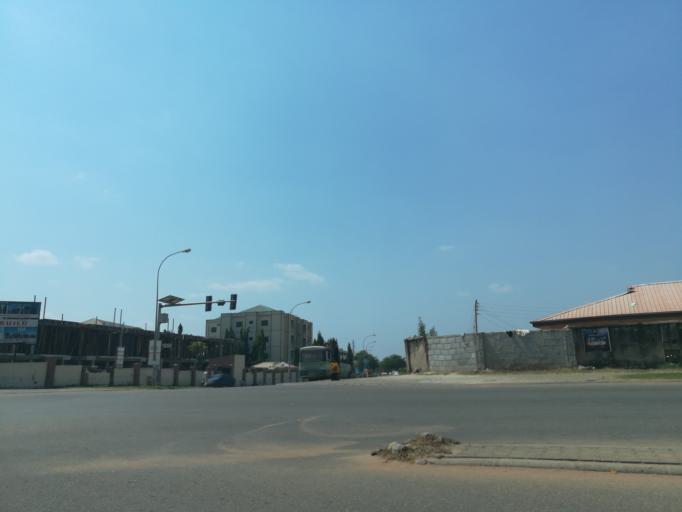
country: NG
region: Abuja Federal Capital Territory
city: Abuja
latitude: 9.0641
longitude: 7.4230
